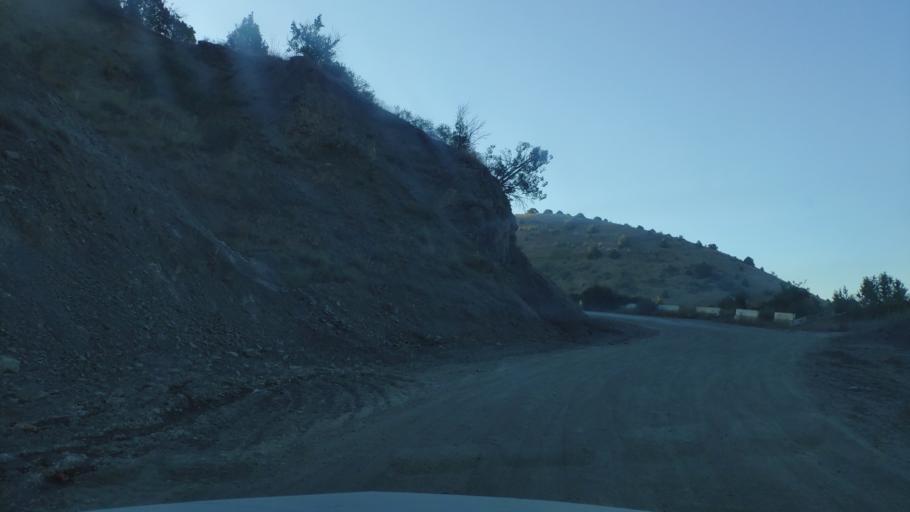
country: TJ
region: Viloyati Sughd
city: Ayni
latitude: 39.6407
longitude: 68.4713
